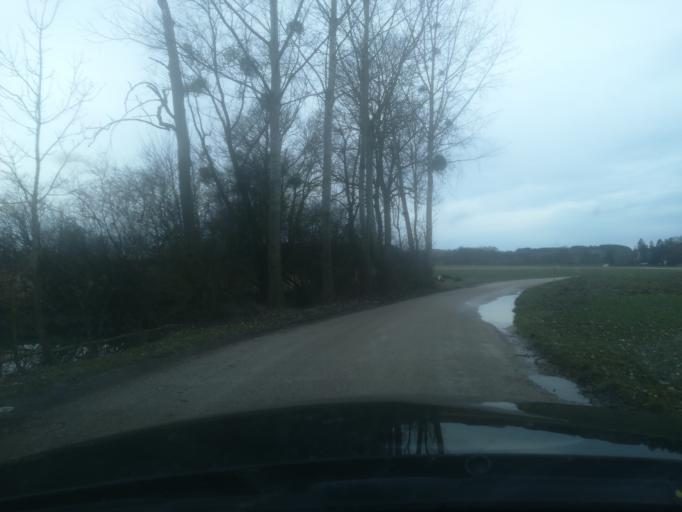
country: AT
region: Upper Austria
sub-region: Wels-Land
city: Gunskirchen
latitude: 48.1650
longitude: 13.9691
